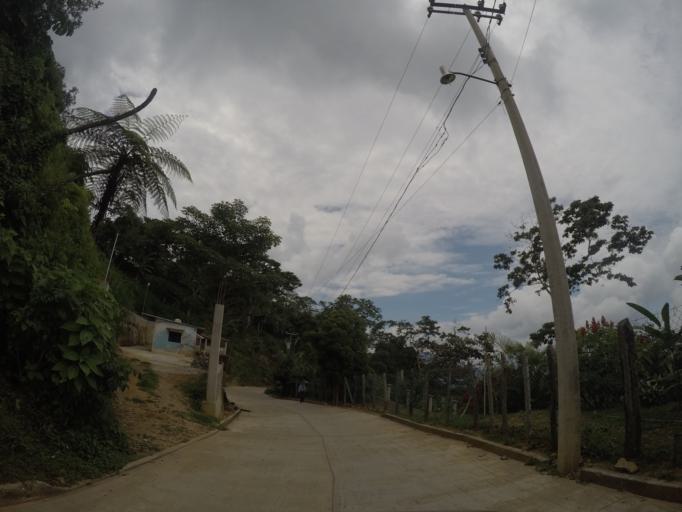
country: MX
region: Oaxaca
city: Pluma Hidalgo
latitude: 15.9227
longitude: -96.4181
